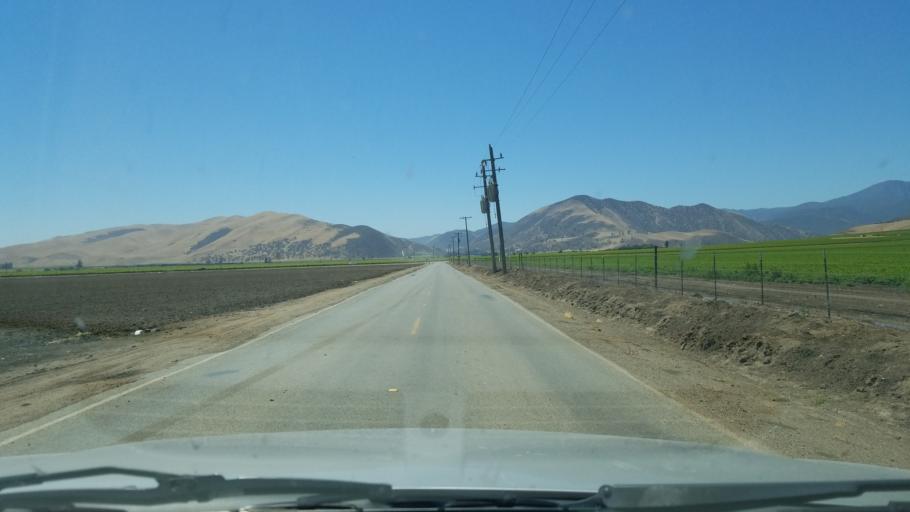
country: US
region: California
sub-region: Monterey County
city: Greenfield
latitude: 36.3196
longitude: -121.3125
